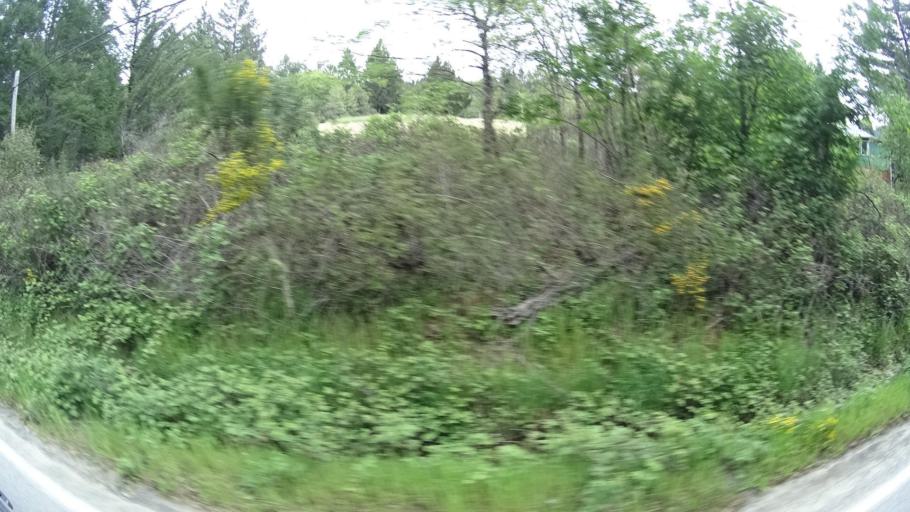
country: US
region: California
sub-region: Humboldt County
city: Redway
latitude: 40.1108
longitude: -123.8938
